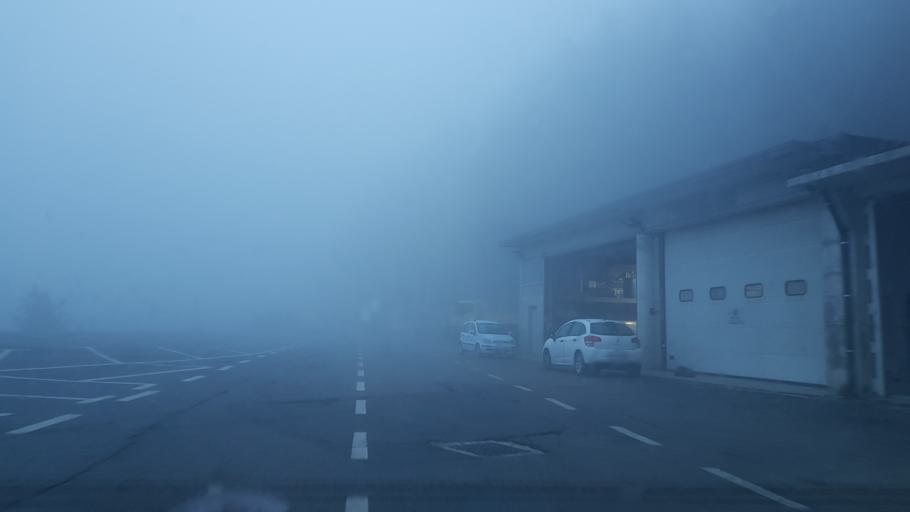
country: IT
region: Piedmont
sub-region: Provincia di Cuneo
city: Frabosa Soprana
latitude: 44.2566
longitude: 7.7791
